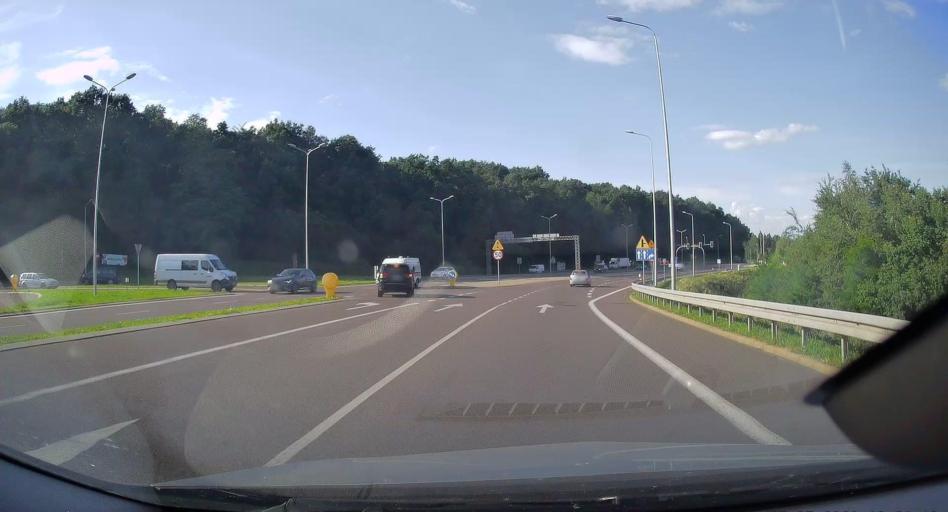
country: PL
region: Subcarpathian Voivodeship
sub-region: Powiat przemyski
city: Zurawica
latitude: 49.8085
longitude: 22.7773
